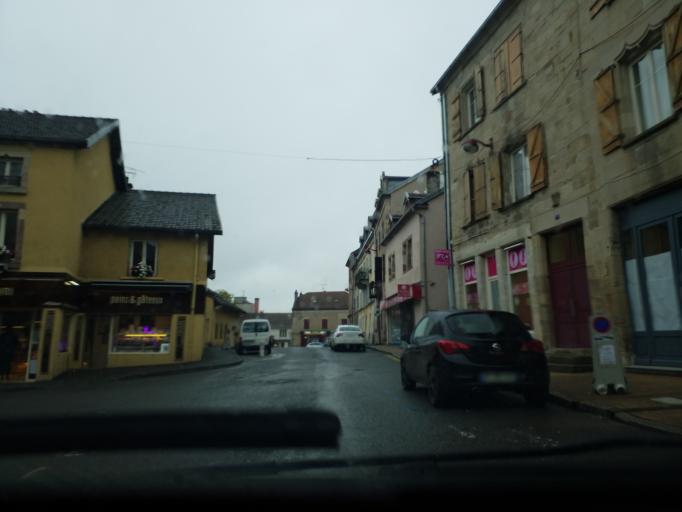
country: FR
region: Franche-Comte
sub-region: Departement de la Haute-Saone
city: Saint-Sauveur
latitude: 47.8170
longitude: 6.3802
